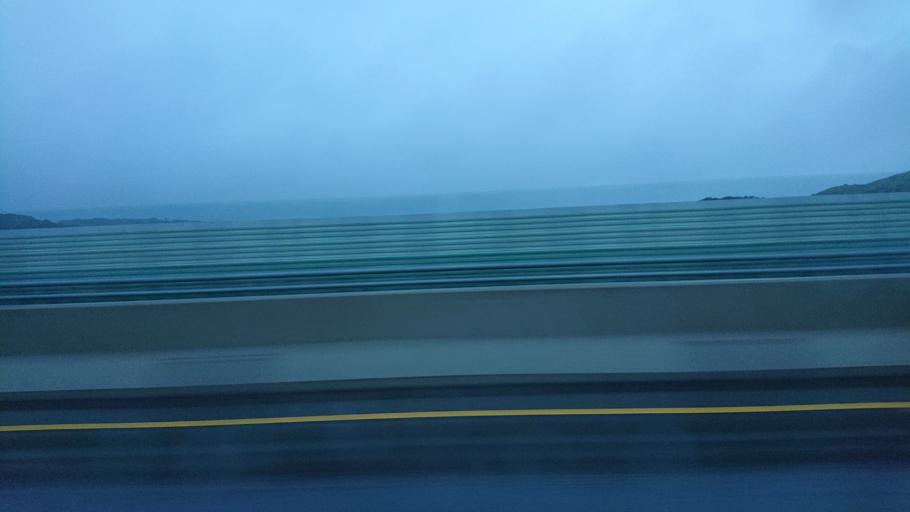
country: TW
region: Taiwan
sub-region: Miaoli
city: Miaoli
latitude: 24.5550
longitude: 120.7102
